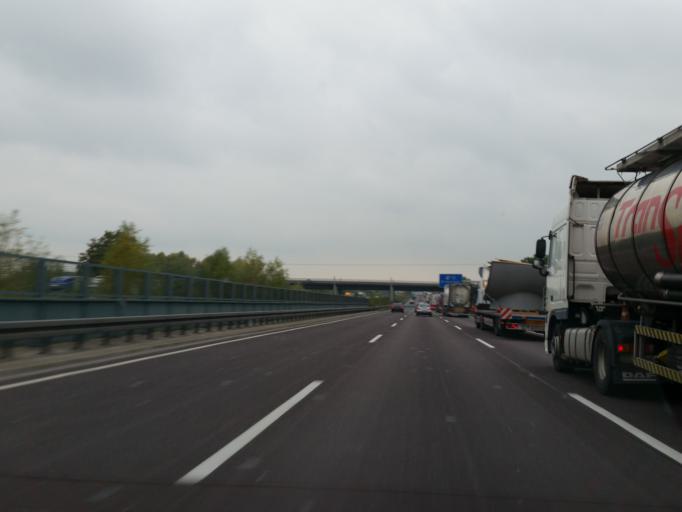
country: DE
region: Lower Saxony
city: Klein Schwulper
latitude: 52.3315
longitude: 10.4432
